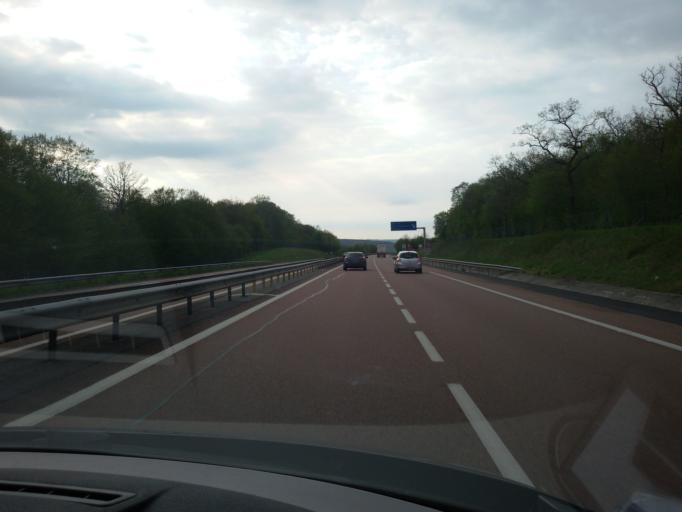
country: FR
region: Champagne-Ardenne
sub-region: Departement de la Haute-Marne
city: Chateauvillain
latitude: 48.0525
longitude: 4.9661
